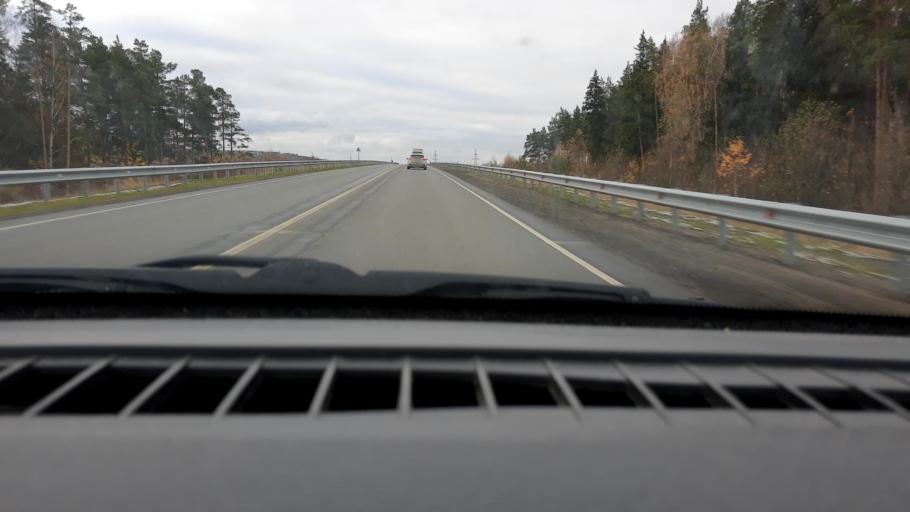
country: RU
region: Nizjnij Novgorod
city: Kstovo
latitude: 56.1564
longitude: 44.1555
